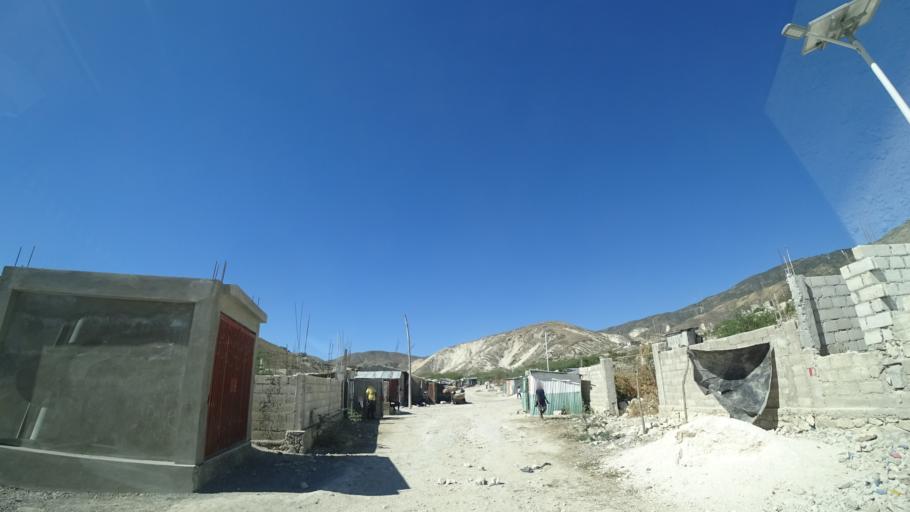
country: HT
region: Ouest
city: Croix des Bouquets
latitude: 18.6713
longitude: -72.2421
